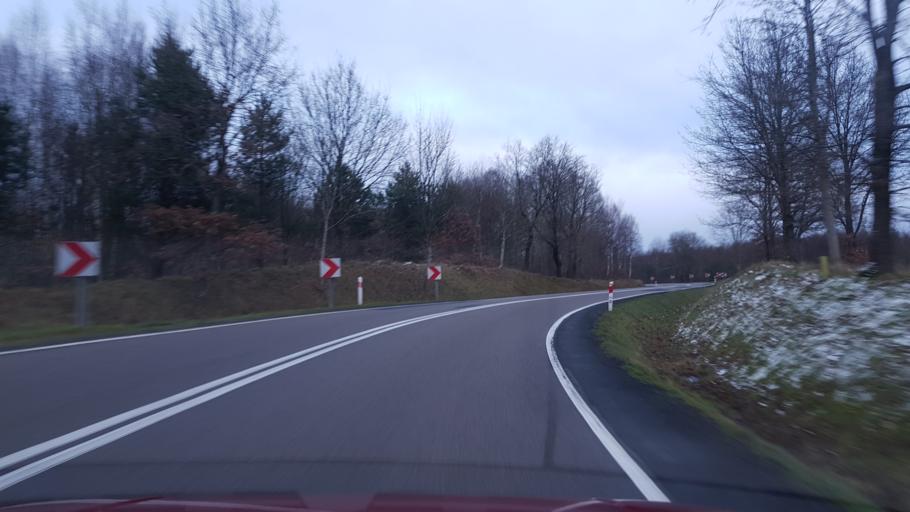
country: PL
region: Pomeranian Voivodeship
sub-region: Powiat bytowski
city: Tuchomie
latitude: 54.0696
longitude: 17.2779
